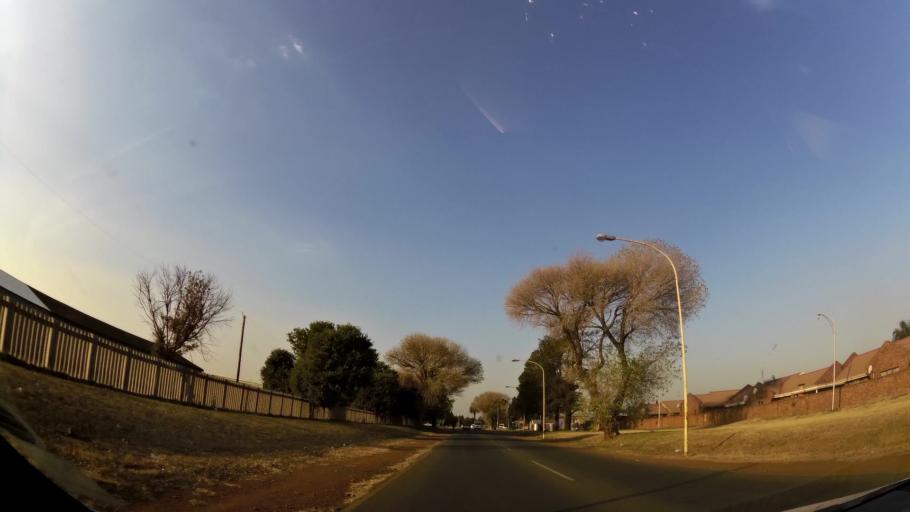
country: ZA
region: Gauteng
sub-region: Ekurhuleni Metropolitan Municipality
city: Springs
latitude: -26.2538
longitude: 28.4012
